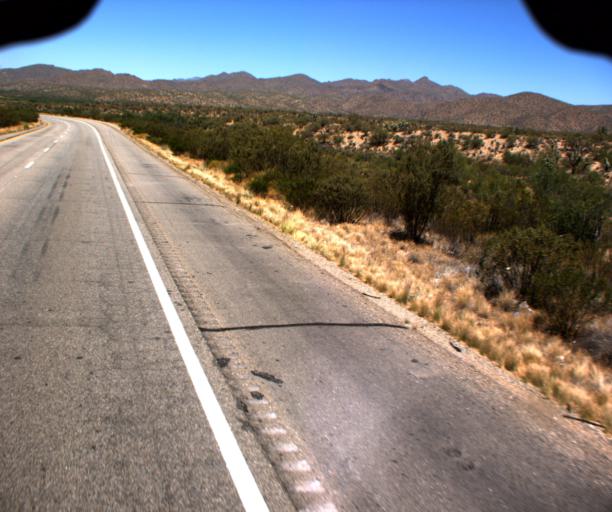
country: US
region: Arizona
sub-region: Yavapai County
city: Bagdad
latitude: 34.3652
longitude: -113.1761
